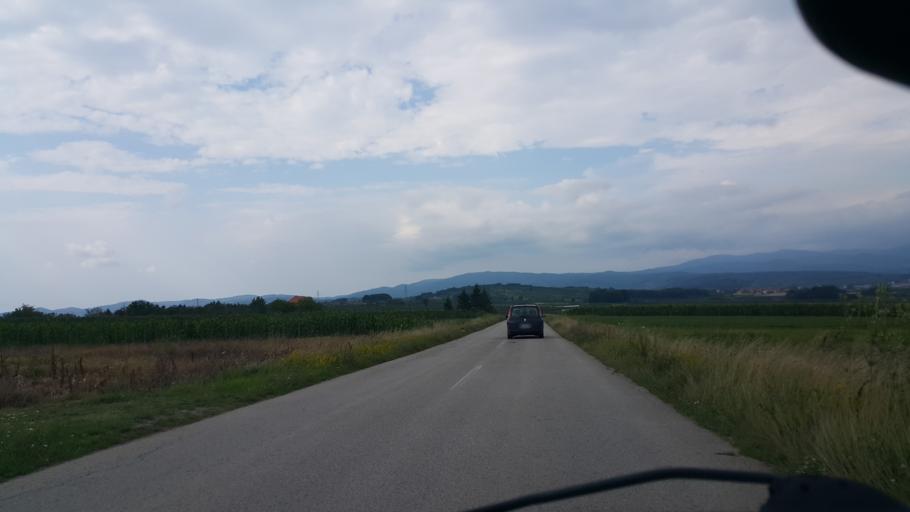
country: RS
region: Central Serbia
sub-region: Toplicki Okrug
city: Blace
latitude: 43.2675
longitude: 21.2735
